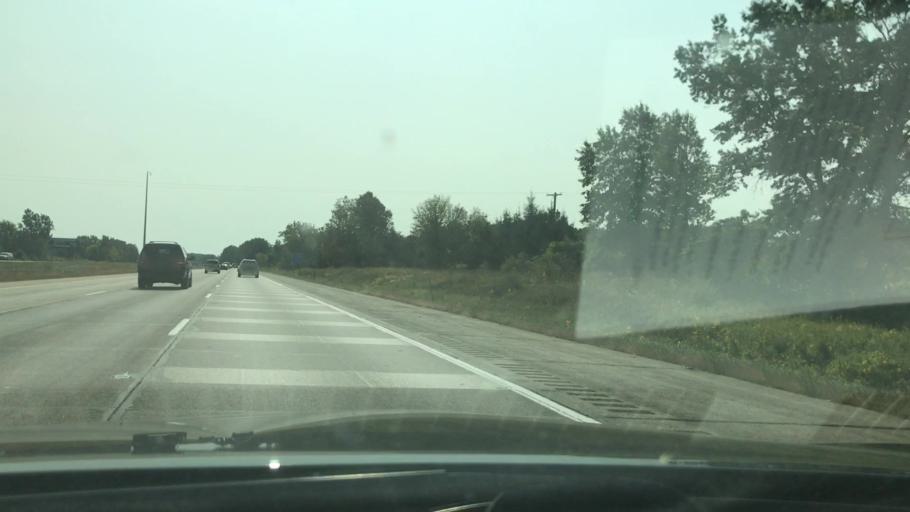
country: US
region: Michigan
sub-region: Livingston County
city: Brighton
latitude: 42.5697
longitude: -83.8444
